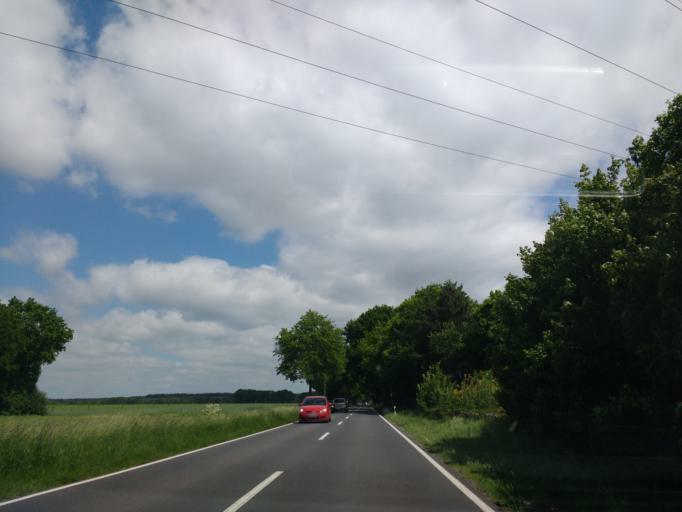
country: DE
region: Lower Saxony
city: Walsrode
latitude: 52.8365
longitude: 9.6412
